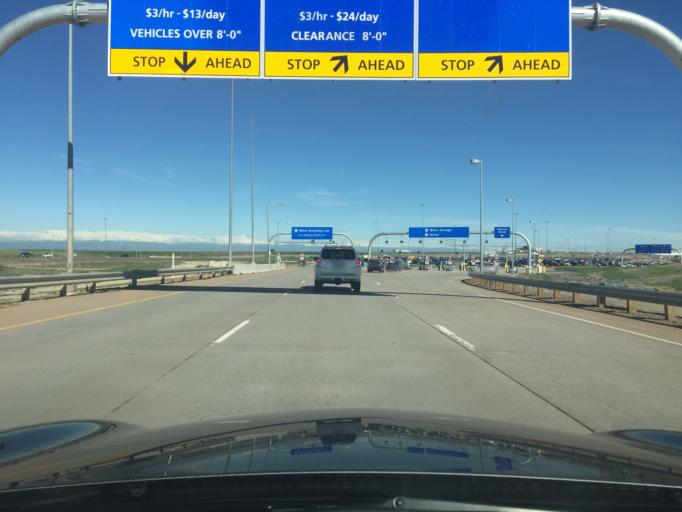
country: US
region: Colorado
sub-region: Weld County
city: Lochbuie
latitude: 39.8434
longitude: -104.6757
